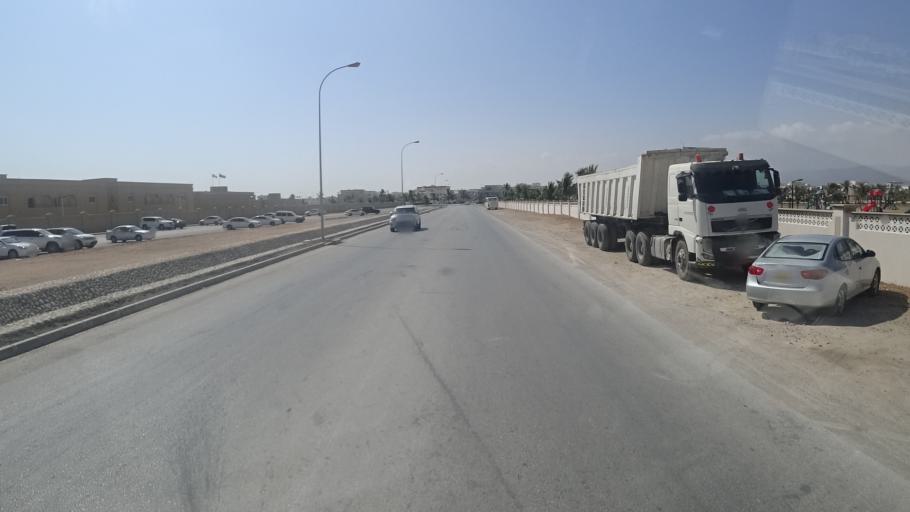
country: OM
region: Zufar
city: Salalah
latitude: 17.0172
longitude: 54.0383
